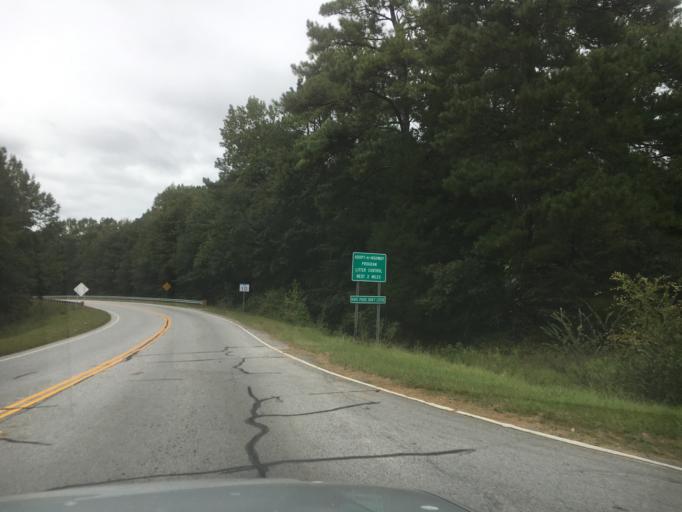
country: US
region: South Carolina
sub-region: McCormick County
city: McCormick
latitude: 34.0527
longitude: -82.2407
